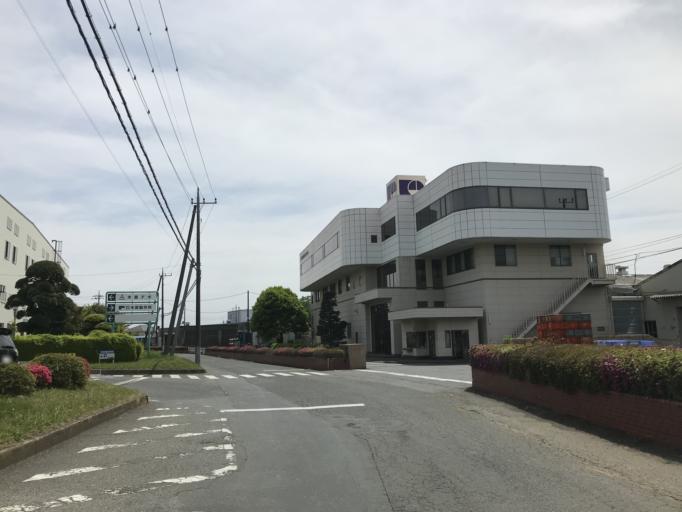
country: JP
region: Ibaraki
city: Mitsukaido
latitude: 35.9856
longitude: 139.9624
